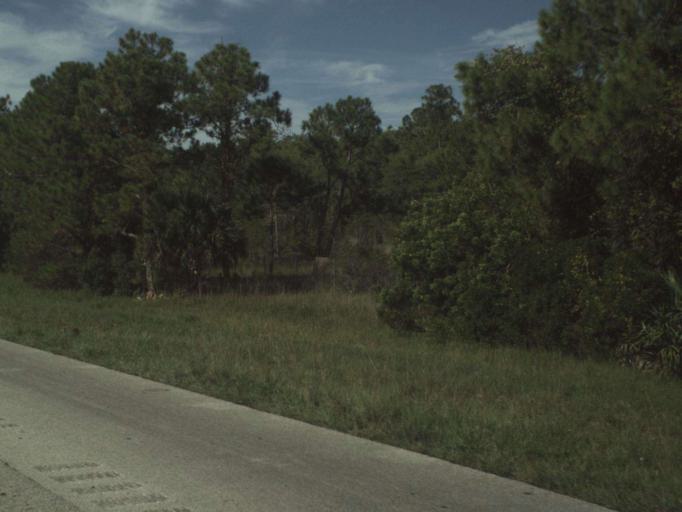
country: US
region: Florida
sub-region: Indian River County
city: Roseland
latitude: 27.8103
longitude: -80.5491
